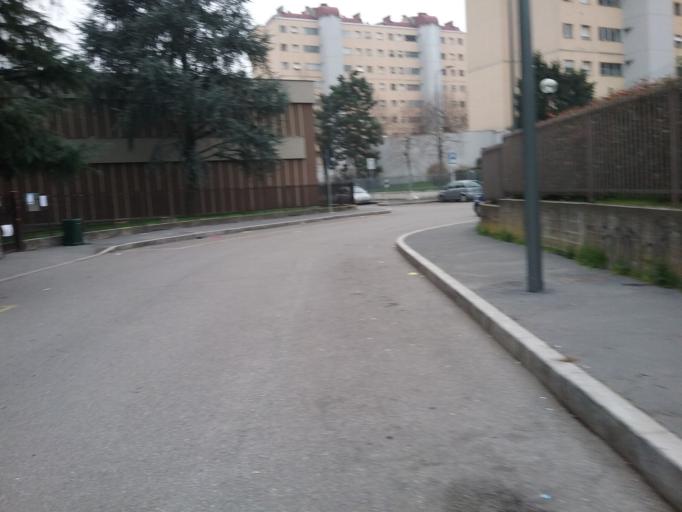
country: IT
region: Lombardy
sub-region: Citta metropolitana di Milano
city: Cesano Boscone
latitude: 45.4739
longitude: 9.1131
